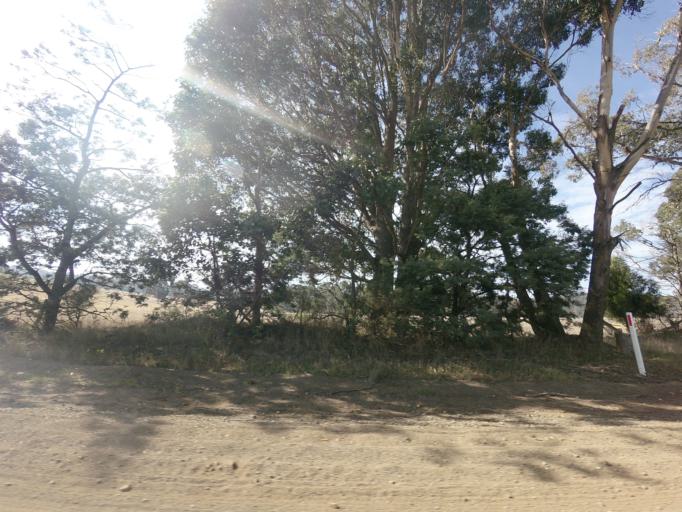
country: AU
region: Tasmania
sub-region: Sorell
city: Sorell
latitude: -42.4750
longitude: 147.4747
